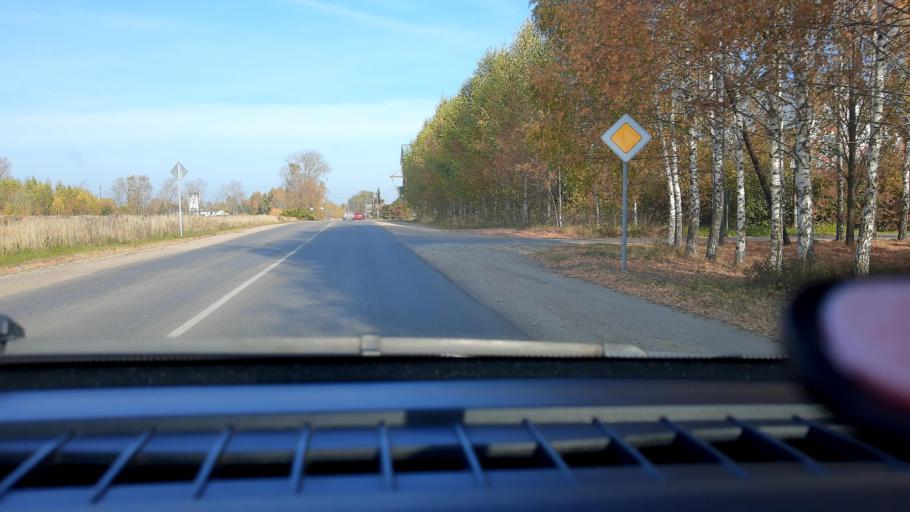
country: RU
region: Nizjnij Novgorod
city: Kstovo
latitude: 56.1494
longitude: 44.2314
